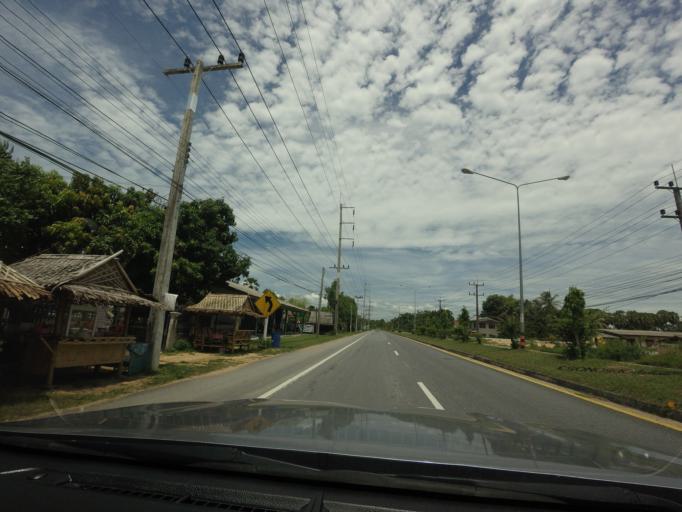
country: TH
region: Songkhla
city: Sathing Phra
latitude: 7.5551
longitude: 100.4140
